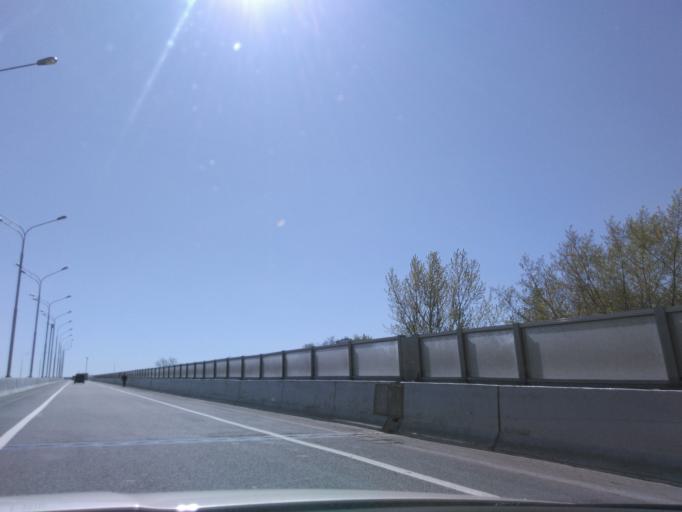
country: RU
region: Moscow
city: Novokhovrino
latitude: 55.8689
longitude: 37.5072
